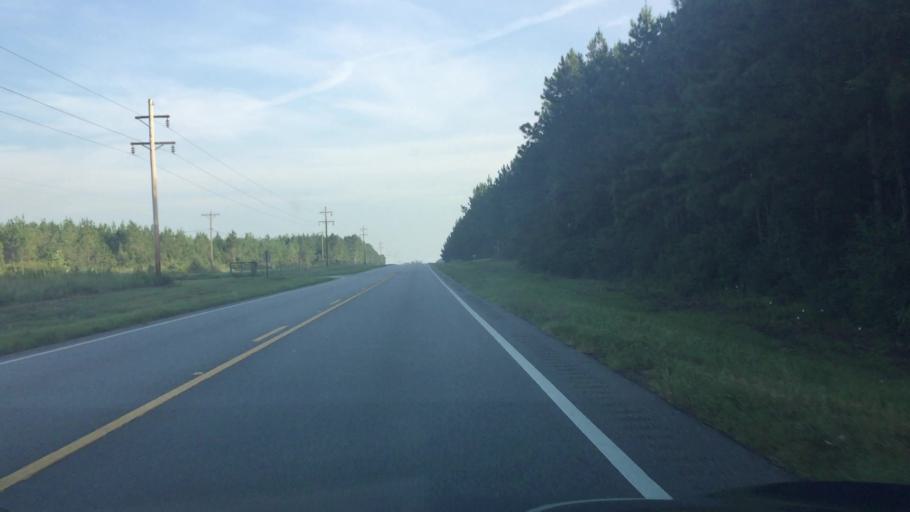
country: US
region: Alabama
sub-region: Covington County
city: Florala
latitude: 31.0390
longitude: -86.3787
